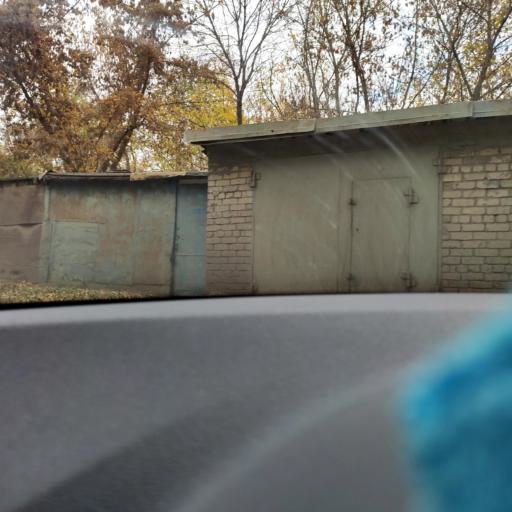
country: RU
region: Samara
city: Samara
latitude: 53.2025
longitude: 50.2504
